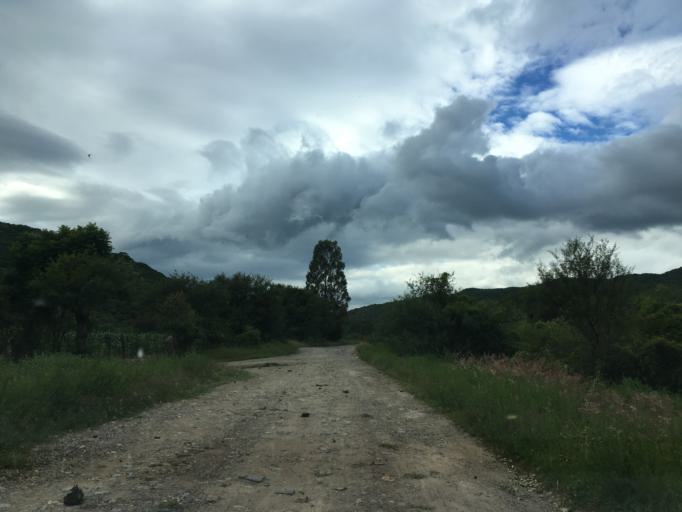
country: MX
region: Guanajuato
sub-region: Acambaro
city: La Ortiga
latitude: 19.9824
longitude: -100.9685
